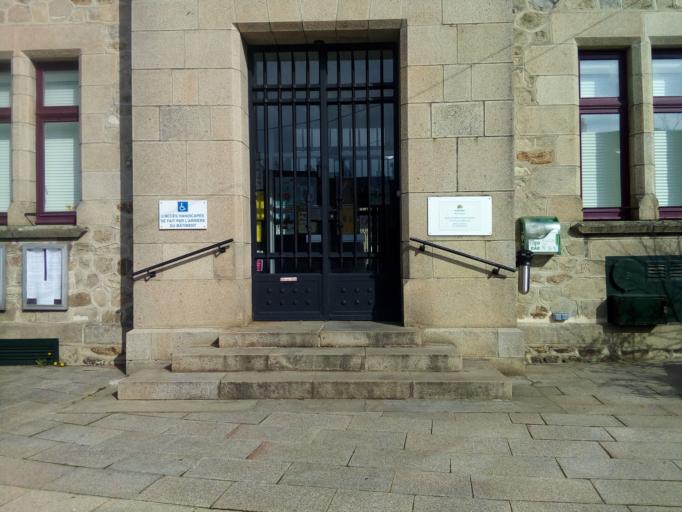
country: FR
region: Limousin
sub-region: Departement de la Creuse
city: Bourganeuf
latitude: 45.9538
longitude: 1.7561
